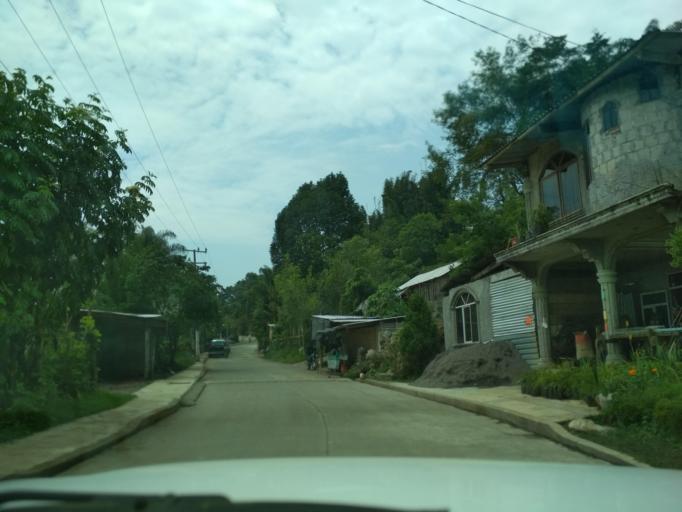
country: MX
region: Veracruz
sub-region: La Perla
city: La Perla
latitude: 18.9282
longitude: -97.1313
